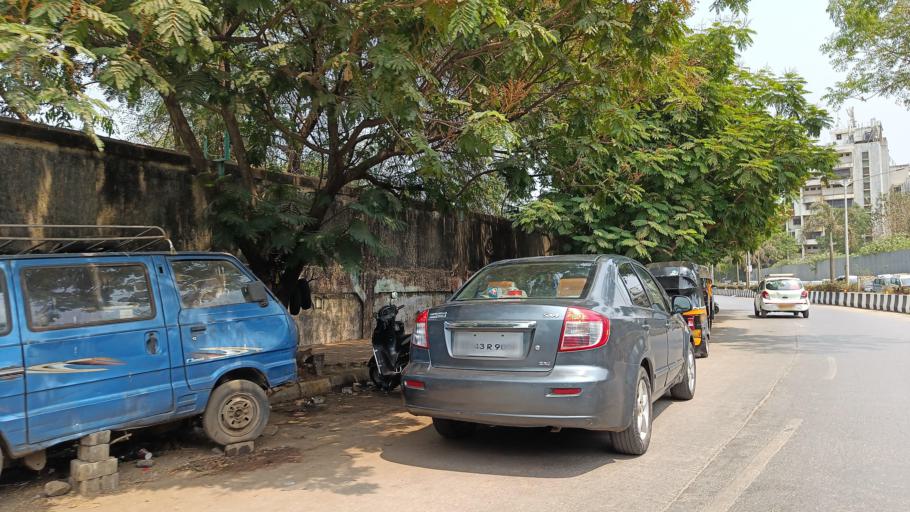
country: IN
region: Maharashtra
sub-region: Mumbai Suburban
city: Mumbai
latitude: 19.0668
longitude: 72.8550
